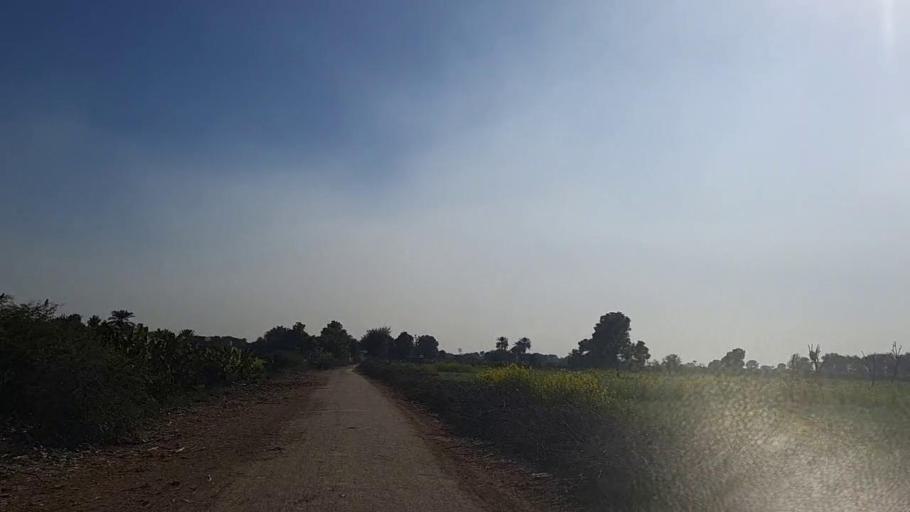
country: PK
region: Sindh
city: Shahpur Chakar
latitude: 26.2088
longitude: 68.6275
